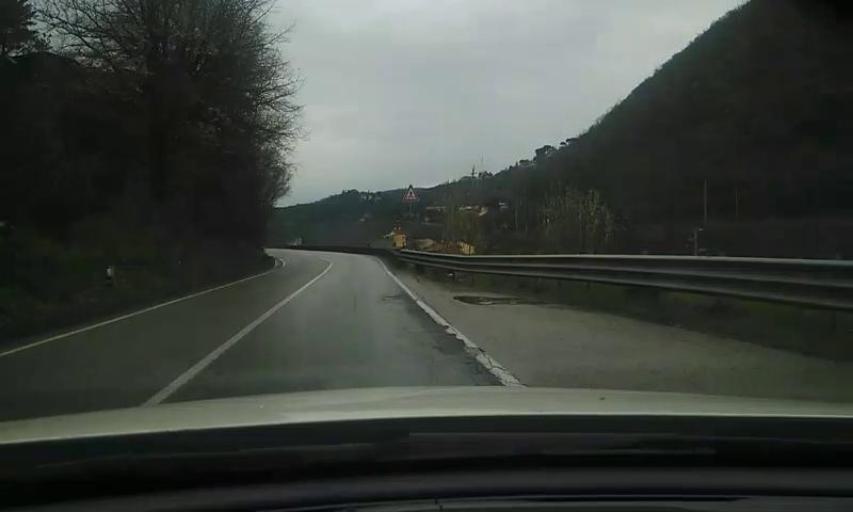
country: IT
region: Tuscany
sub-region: Provincia di Prato
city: Vaiano
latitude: 43.9194
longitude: 11.1264
